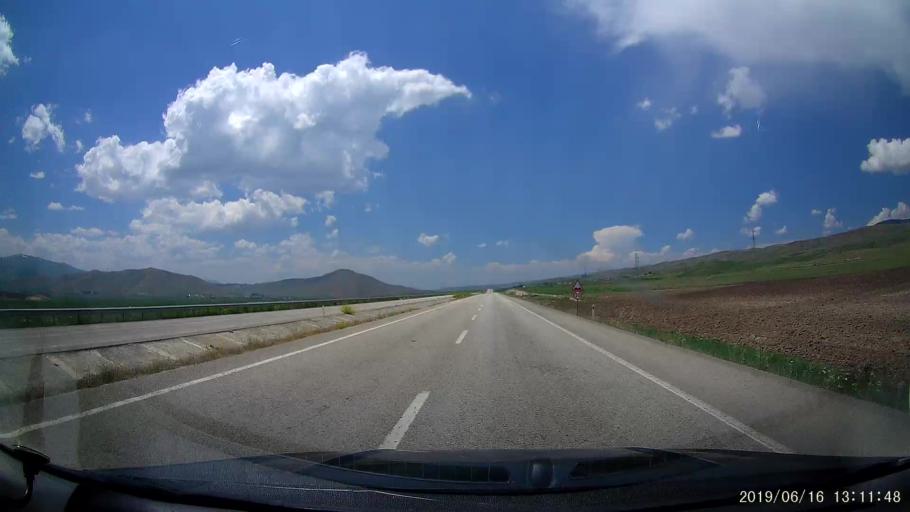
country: TR
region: Agri
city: Diyadin
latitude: 39.5939
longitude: 43.5972
